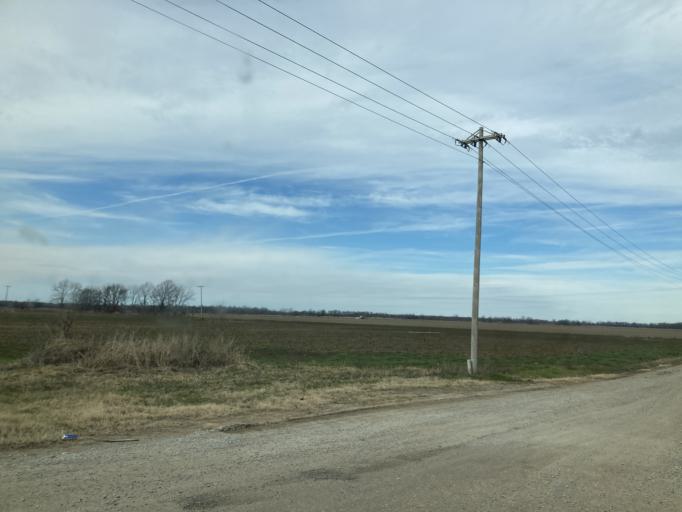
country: US
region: Mississippi
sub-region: Washington County
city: Hollandale
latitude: 33.1838
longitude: -90.6886
